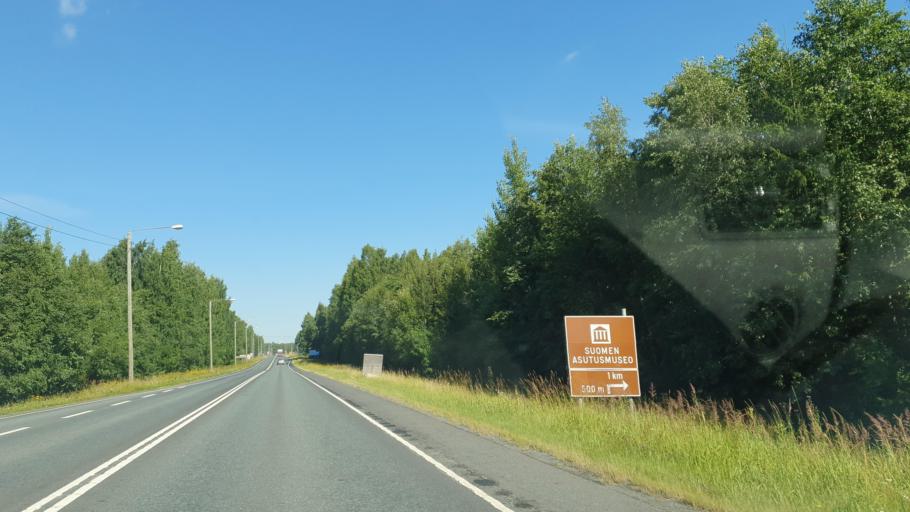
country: FI
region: Northern Savo
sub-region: Kuopio
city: Siilinjaervi
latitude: 63.1963
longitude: 27.5401
